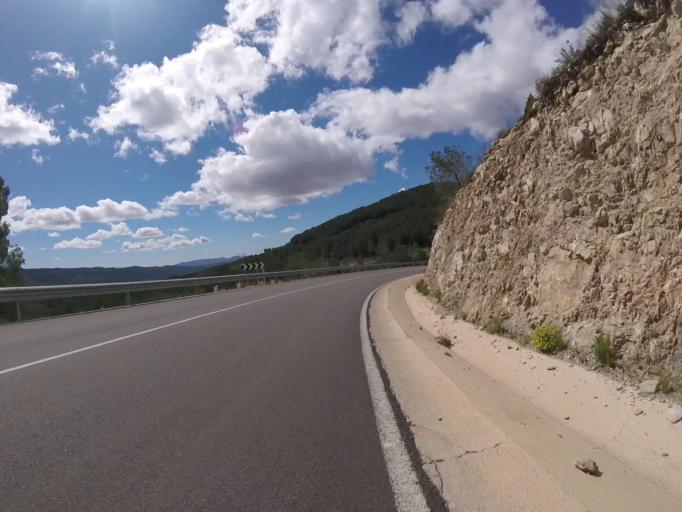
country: ES
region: Valencia
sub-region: Provincia de Castello
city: Adzaneta
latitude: 40.2725
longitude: -0.1099
